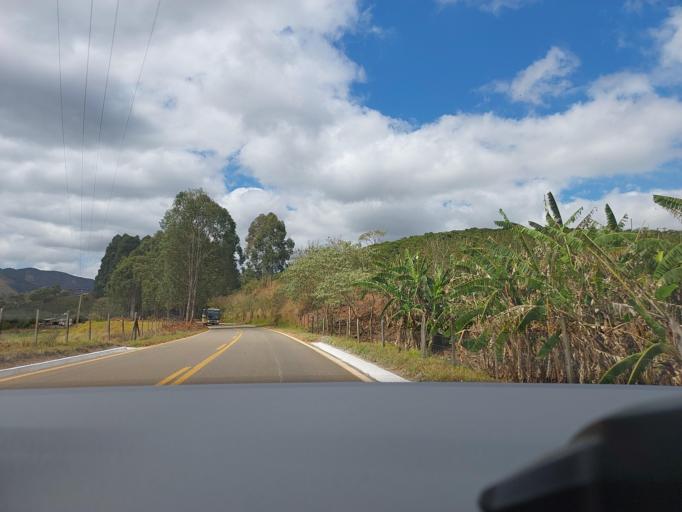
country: BR
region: Minas Gerais
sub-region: Visconde Do Rio Branco
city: Visconde do Rio Branco
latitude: -20.9456
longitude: -42.6246
